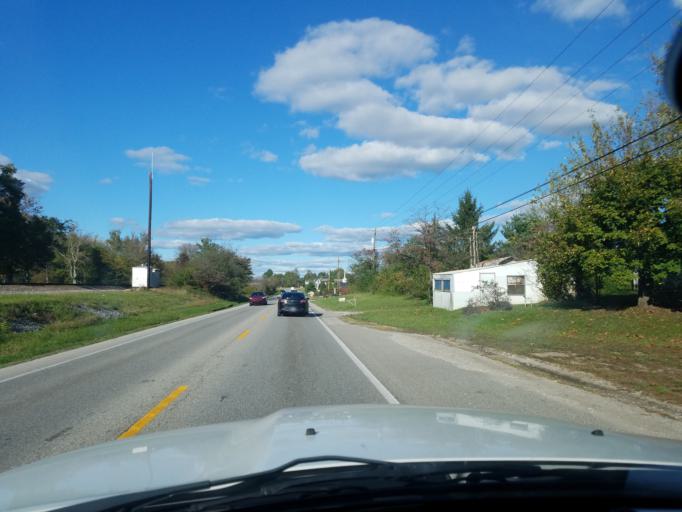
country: US
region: Kentucky
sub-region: Laurel County
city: London
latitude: 37.0429
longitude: -84.0549
